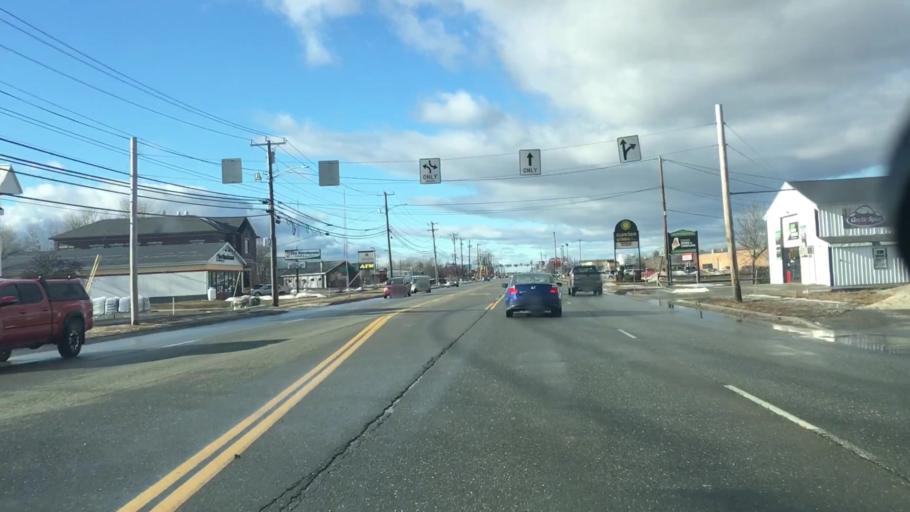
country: US
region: Maine
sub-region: Penobscot County
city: Brewer
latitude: 44.7785
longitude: -68.7380
